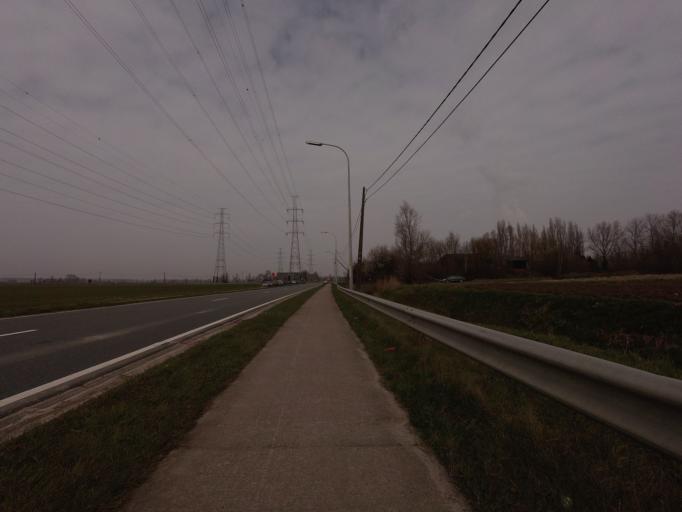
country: BE
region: Flanders
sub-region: Provincie Oost-Vlaanderen
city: Beveren
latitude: 51.3073
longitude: 4.2533
